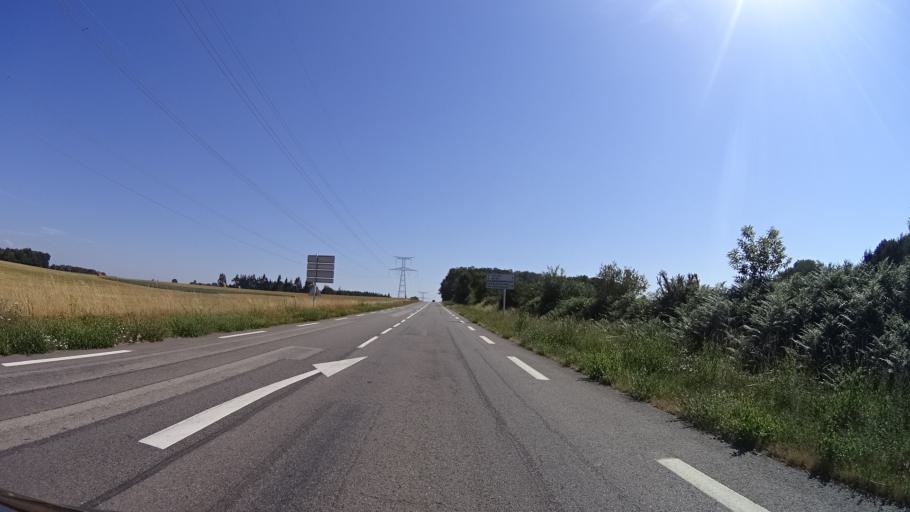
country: FR
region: Brittany
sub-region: Departement du Morbihan
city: Saint-Dolay
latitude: 47.5610
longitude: -2.1329
